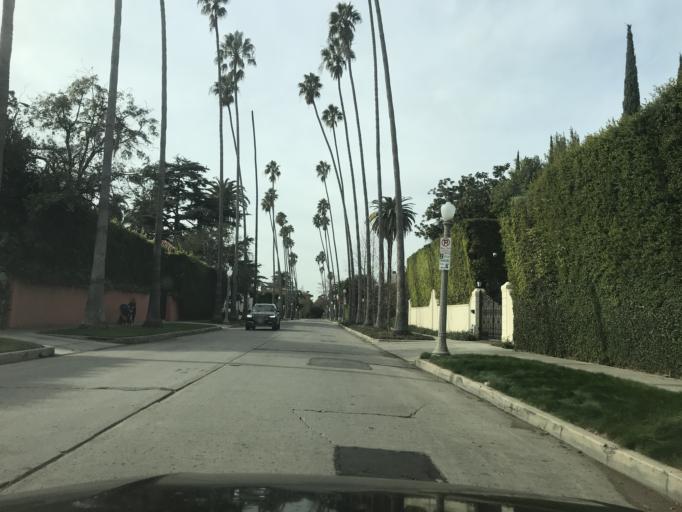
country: US
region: California
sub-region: Los Angeles County
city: Hollywood
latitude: 34.0654
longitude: -118.3205
